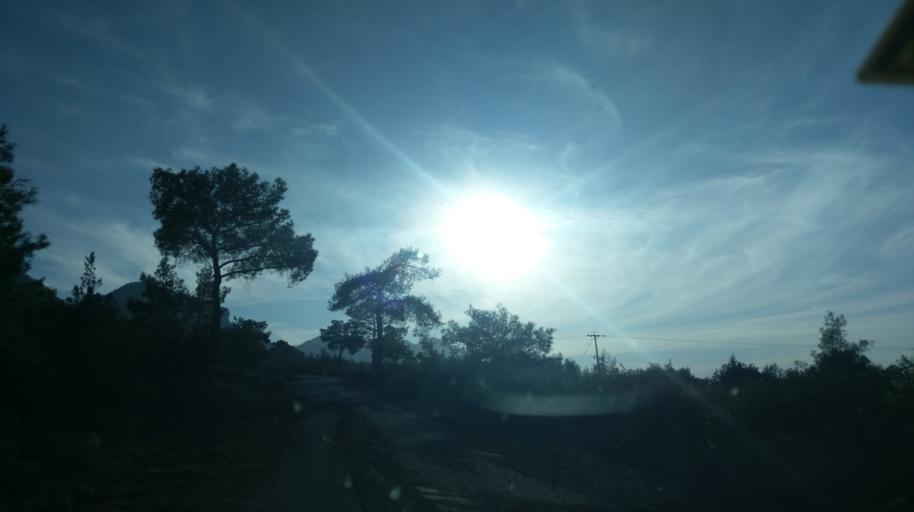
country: CY
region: Ammochostos
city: Lefkonoiko
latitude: 35.3286
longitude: 33.5919
